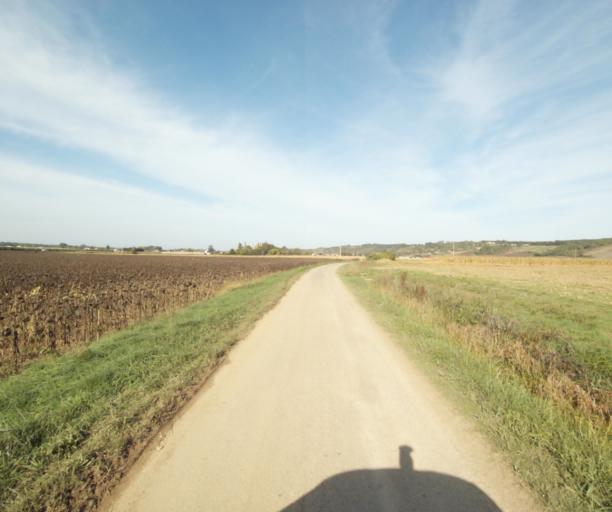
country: FR
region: Midi-Pyrenees
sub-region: Departement du Tarn-et-Garonne
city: Orgueil
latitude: 43.9167
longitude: 1.4329
